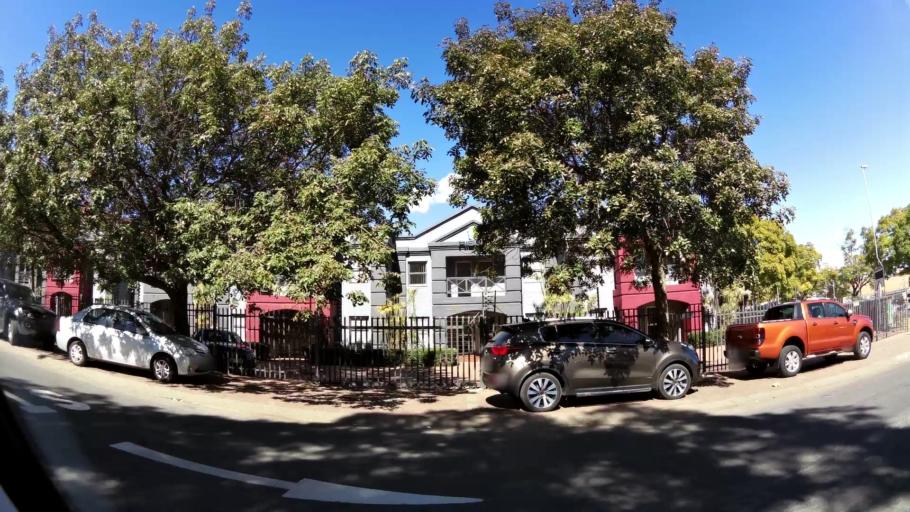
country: ZA
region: Limpopo
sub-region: Capricorn District Municipality
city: Polokwane
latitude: -23.9154
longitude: 29.4563
